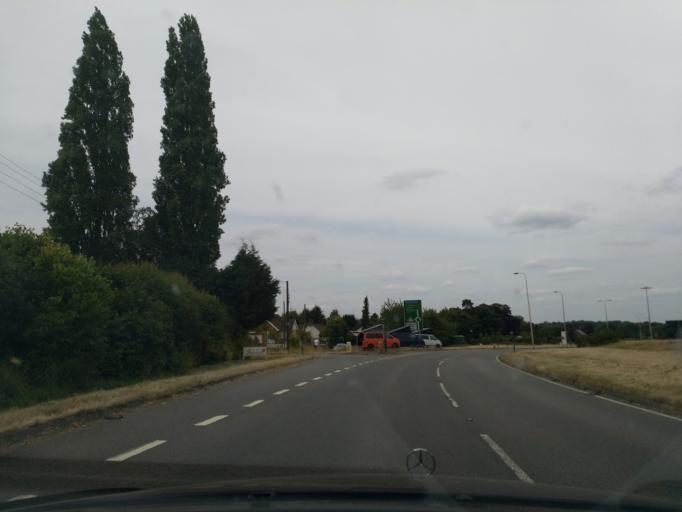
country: GB
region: England
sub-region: Solihull
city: Barston
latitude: 52.4113
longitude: -1.6712
